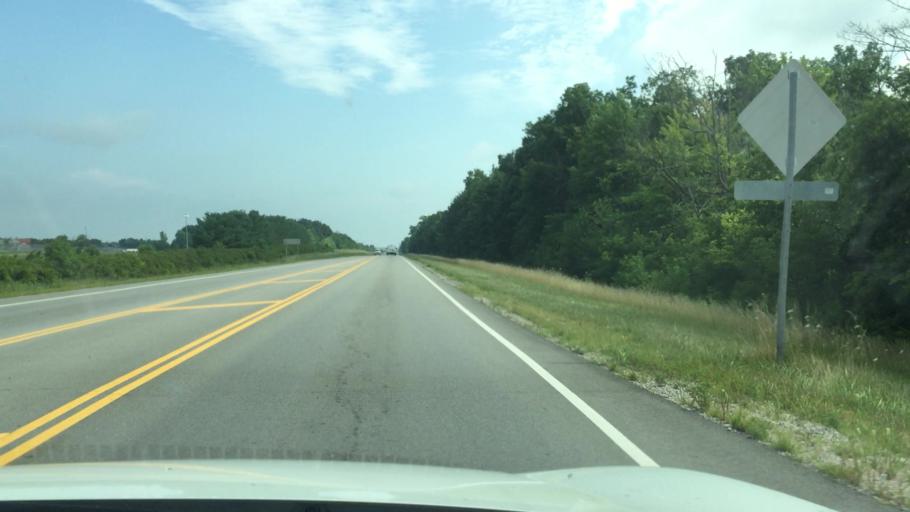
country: US
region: Ohio
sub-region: Union County
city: Marysville
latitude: 40.2273
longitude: -83.3979
